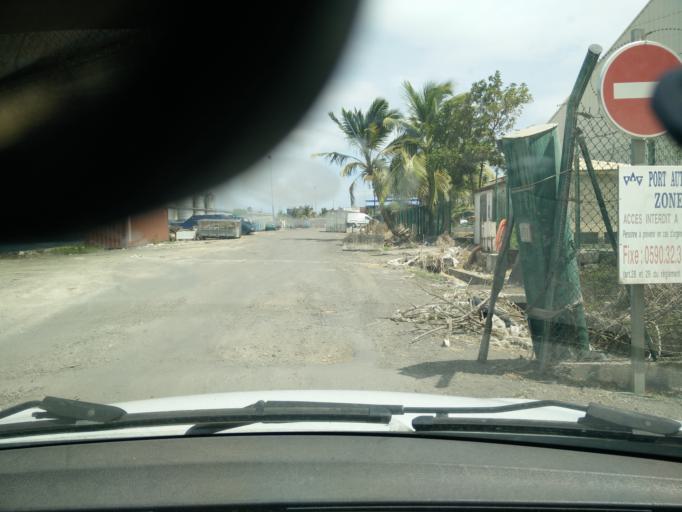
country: GP
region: Guadeloupe
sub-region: Guadeloupe
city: Pointe-a-Pitre
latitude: 16.2347
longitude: -61.5509
